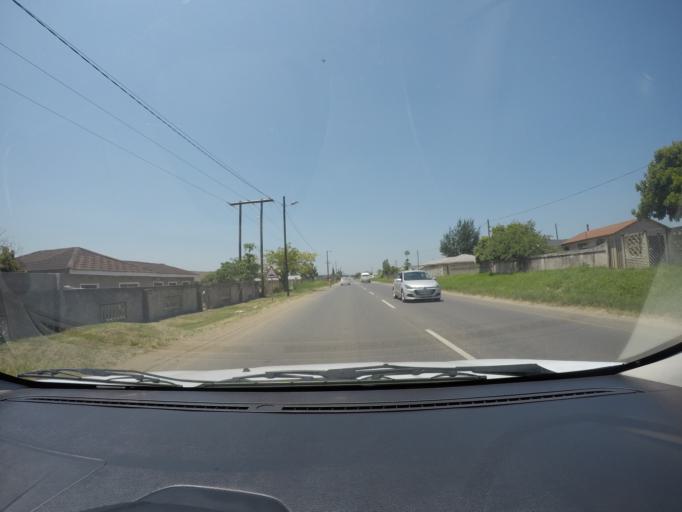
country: ZA
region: KwaZulu-Natal
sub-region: uThungulu District Municipality
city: eSikhawini
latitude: -28.8828
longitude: 31.8881
